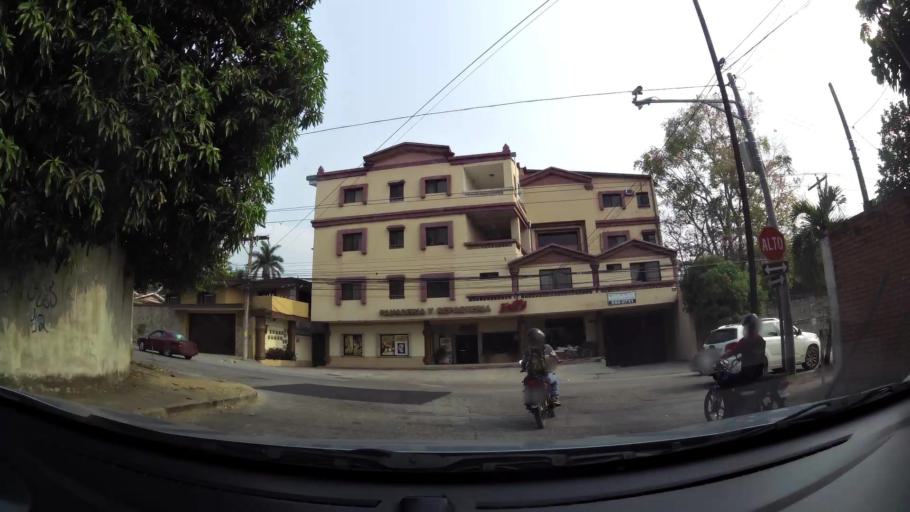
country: HN
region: Cortes
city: Armenta
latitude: 15.4979
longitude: -88.0461
